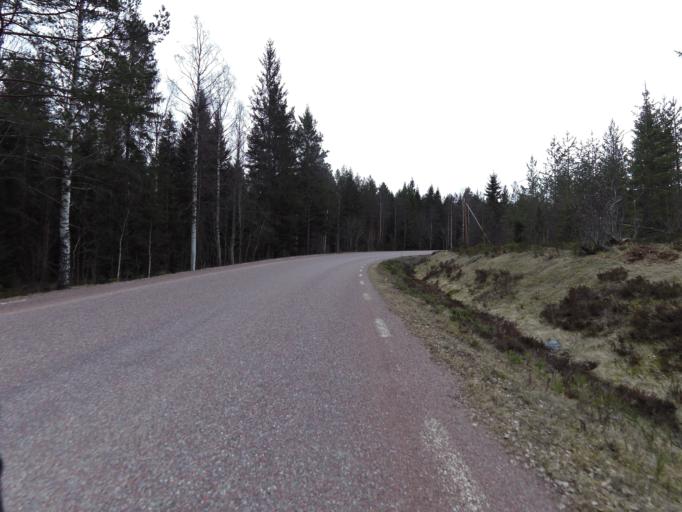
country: SE
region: Gaevleborg
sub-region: Hofors Kommun
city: Hofors
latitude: 60.4847
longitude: 16.4168
